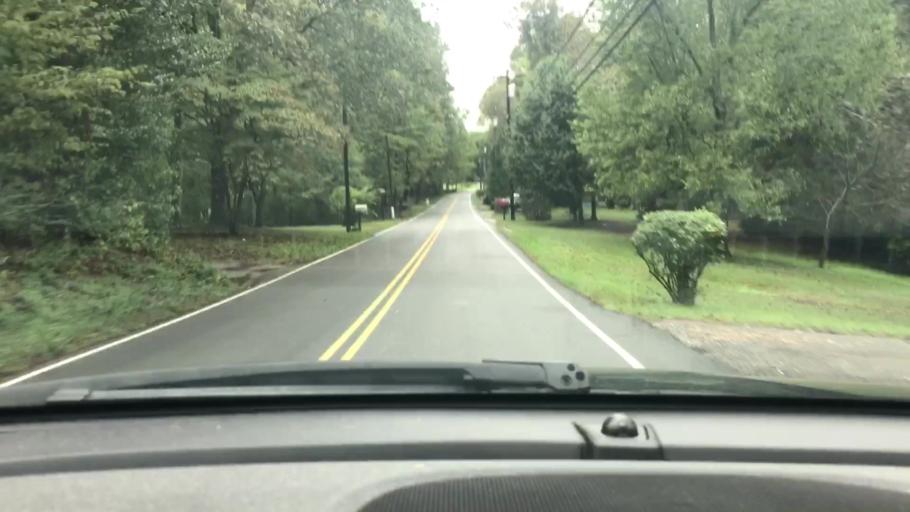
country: US
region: Tennessee
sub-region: Cheatham County
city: Kingston Springs
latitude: 36.1085
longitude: -87.1396
